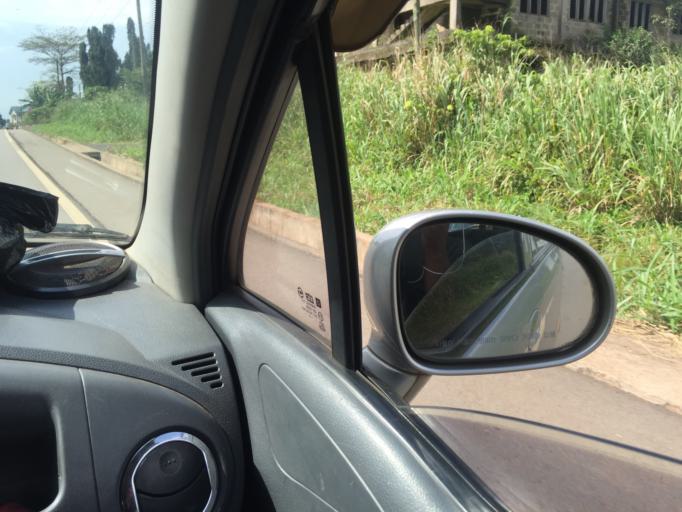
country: GH
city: Mpraeso
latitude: 6.5772
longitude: -0.7298
